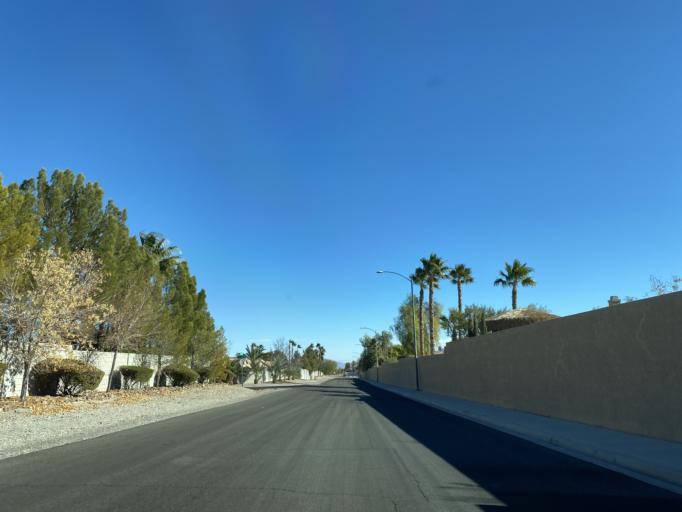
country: US
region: Nevada
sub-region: Clark County
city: Summerlin South
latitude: 36.2666
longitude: -115.2773
